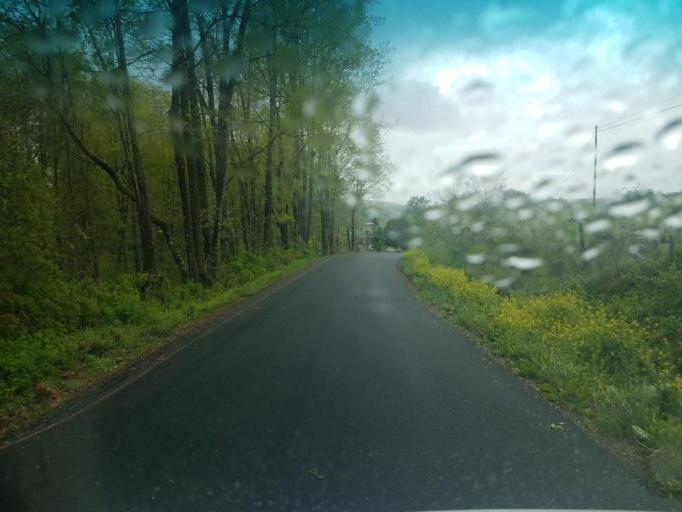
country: US
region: Virginia
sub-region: Smyth County
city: Marion
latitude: 36.9330
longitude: -81.5316
